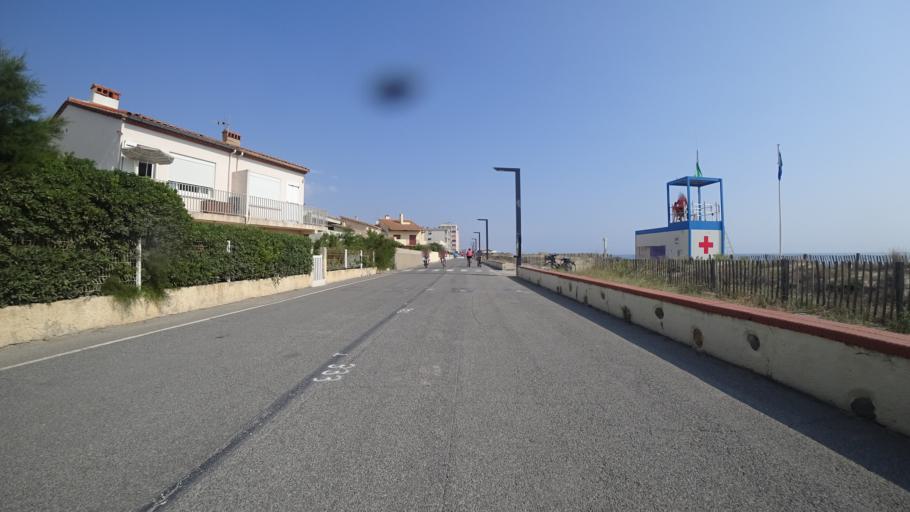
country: FR
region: Languedoc-Roussillon
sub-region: Departement des Pyrenees-Orientales
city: Saint-Cyprien-Plage
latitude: 42.6274
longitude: 3.0360
